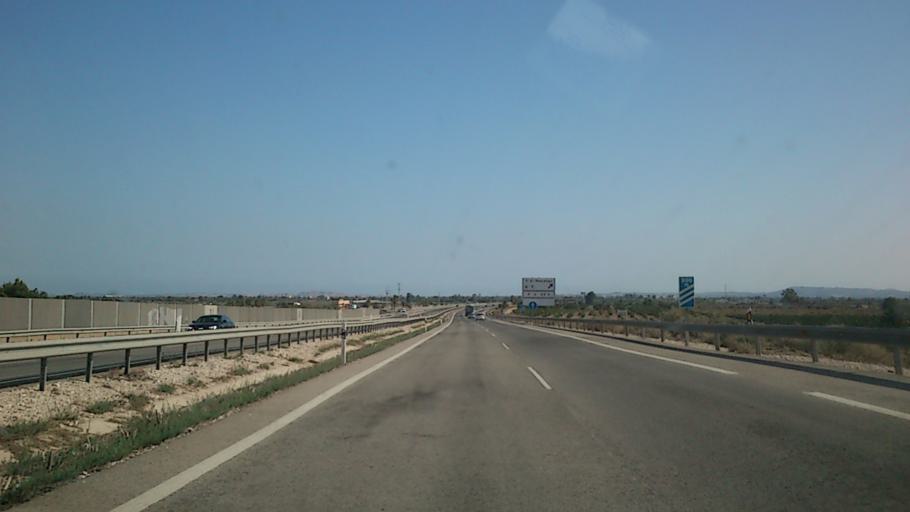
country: ES
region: Valencia
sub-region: Provincia de Alicante
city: San Isidro
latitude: 38.2007
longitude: -0.8153
